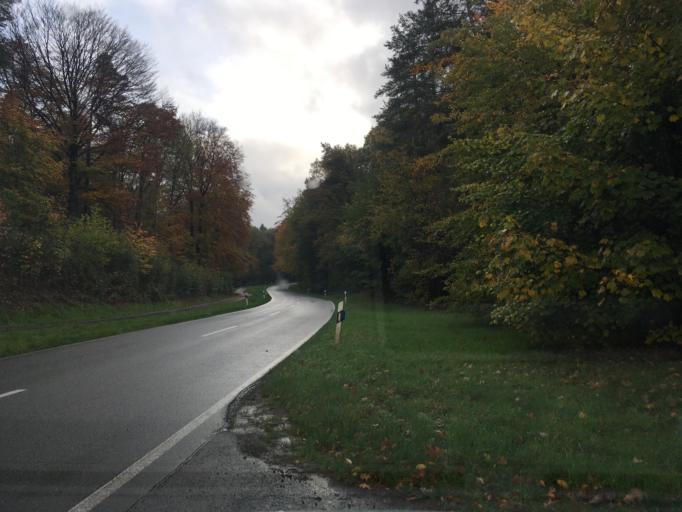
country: DE
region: North Rhine-Westphalia
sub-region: Regierungsbezirk Munster
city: Klein Reken
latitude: 51.8450
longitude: 7.0301
